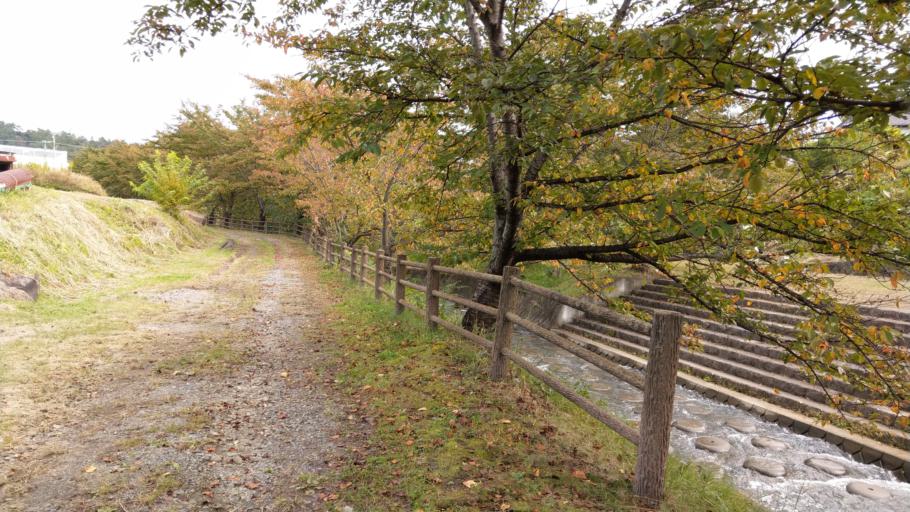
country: JP
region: Nagano
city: Komoro
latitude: 36.3348
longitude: 138.4114
